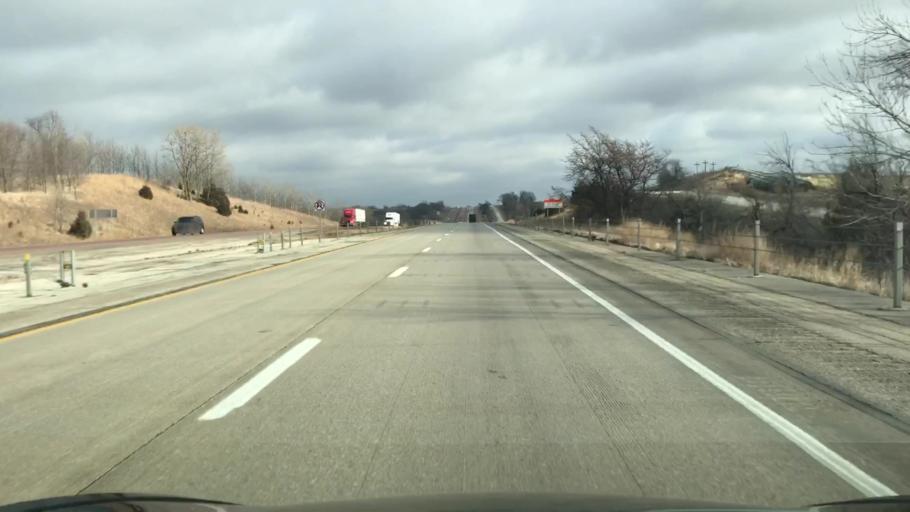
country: US
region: Iowa
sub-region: Guthrie County
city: Guthrie Center
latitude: 41.4964
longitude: -94.5442
